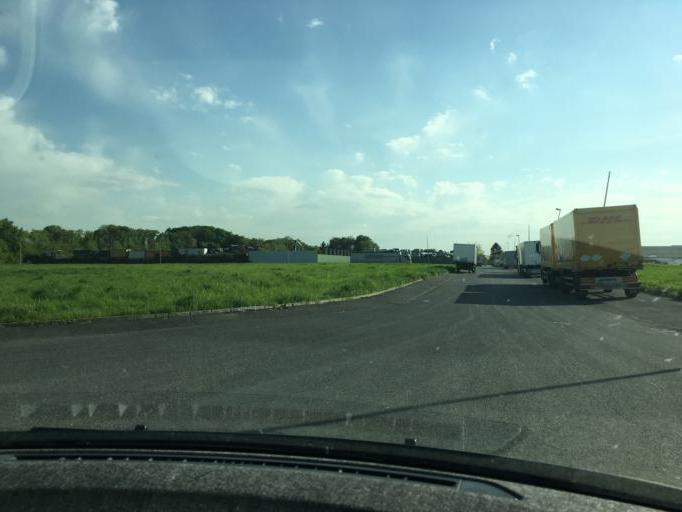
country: DE
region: North Rhine-Westphalia
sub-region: Regierungsbezirk Koln
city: Mengenich
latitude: 50.9827
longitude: 6.8501
